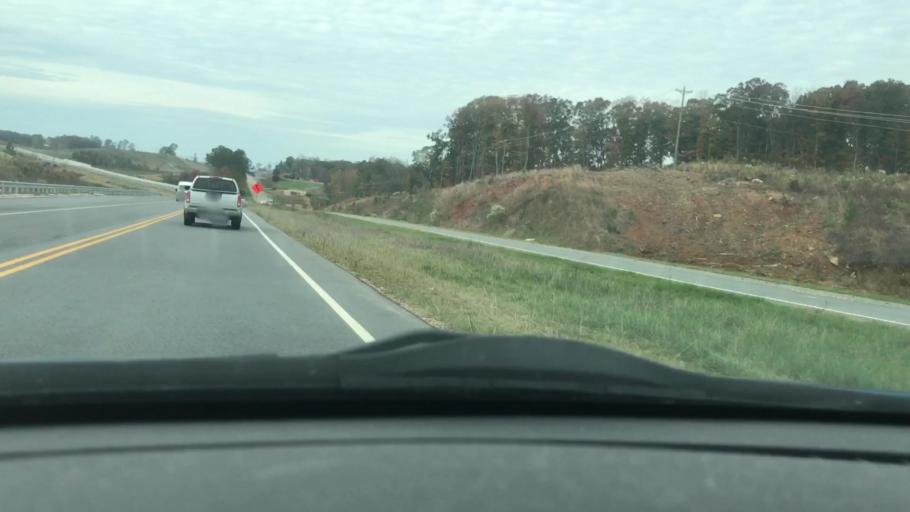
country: US
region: North Carolina
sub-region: Randolph County
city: Asheboro
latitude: 35.6956
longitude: -79.8607
